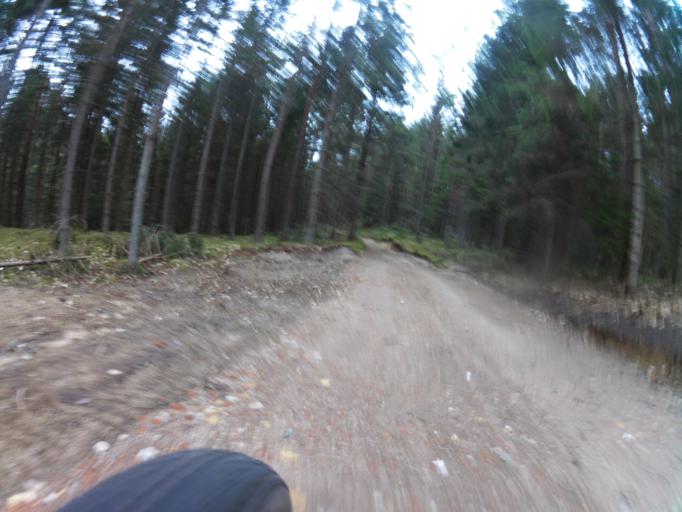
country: PL
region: West Pomeranian Voivodeship
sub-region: Powiat koszalinski
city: Polanow
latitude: 54.1844
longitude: 16.6783
